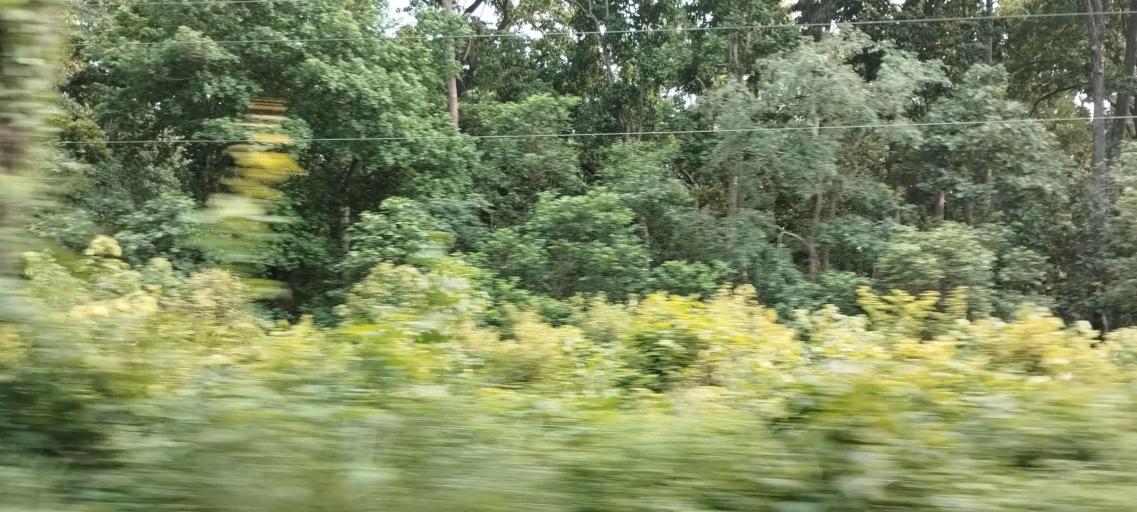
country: NP
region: Mid Western
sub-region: Bheri Zone
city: Bardiya
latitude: 28.4313
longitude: 81.3655
